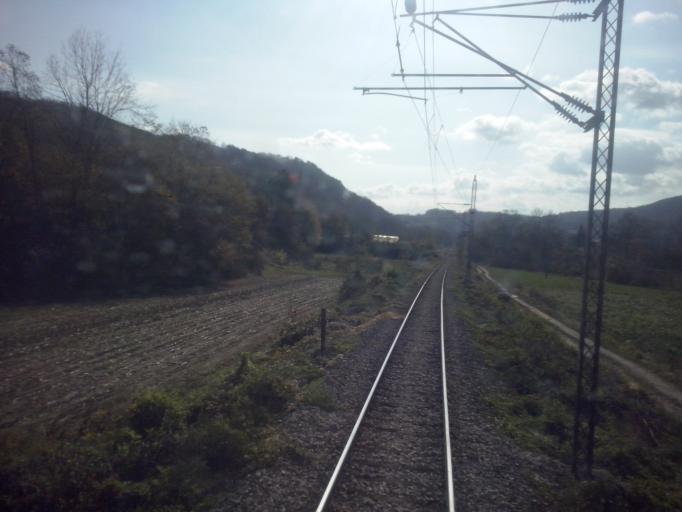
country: RS
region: Central Serbia
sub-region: Zlatiborski Okrug
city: Pozega
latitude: 43.9333
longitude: 19.9884
